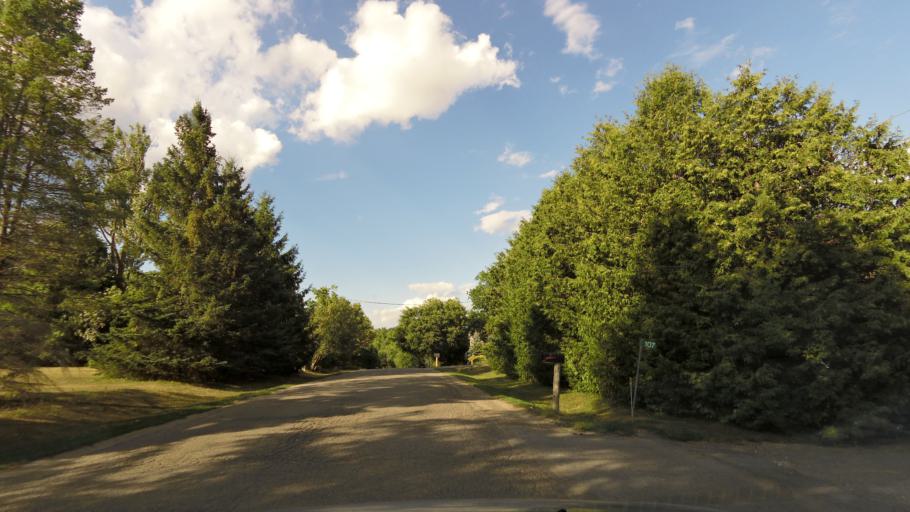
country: CA
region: Ontario
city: Brampton
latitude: 43.7636
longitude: -79.9259
